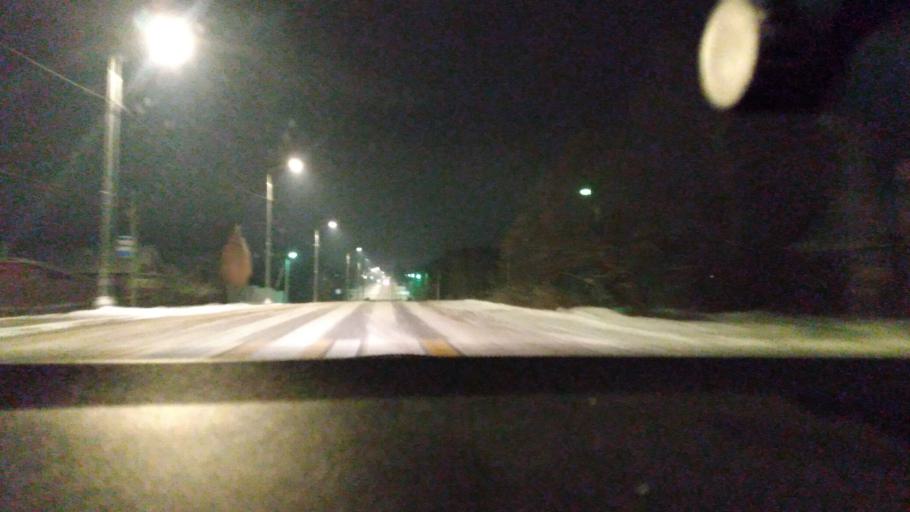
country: RU
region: Moskovskaya
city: Lukhovitsy
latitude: 55.0932
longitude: 38.9544
